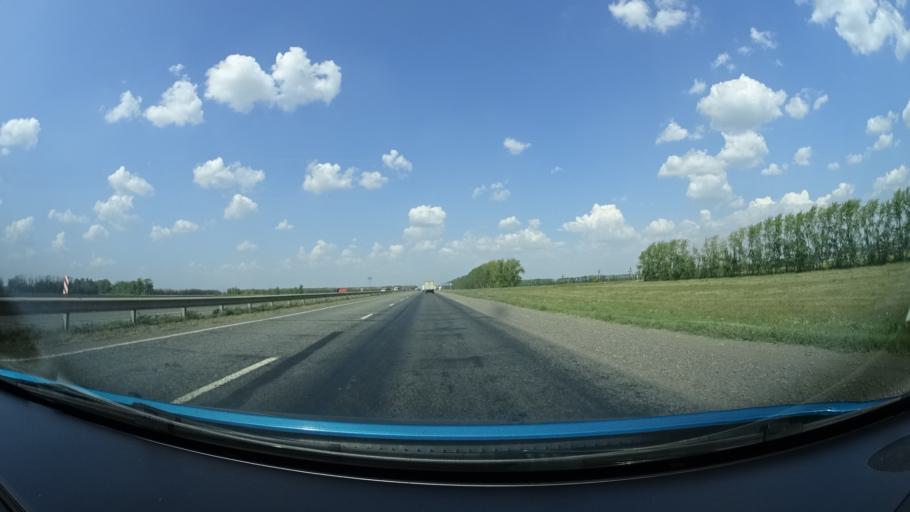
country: RU
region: Bashkortostan
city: Dmitriyevka
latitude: 54.6914
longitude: 55.2928
